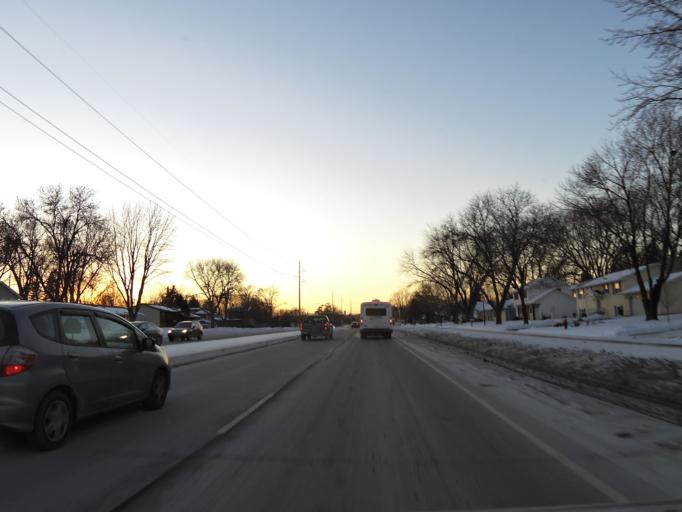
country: US
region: Minnesota
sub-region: Dakota County
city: Apple Valley
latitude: 44.7320
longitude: -93.2417
